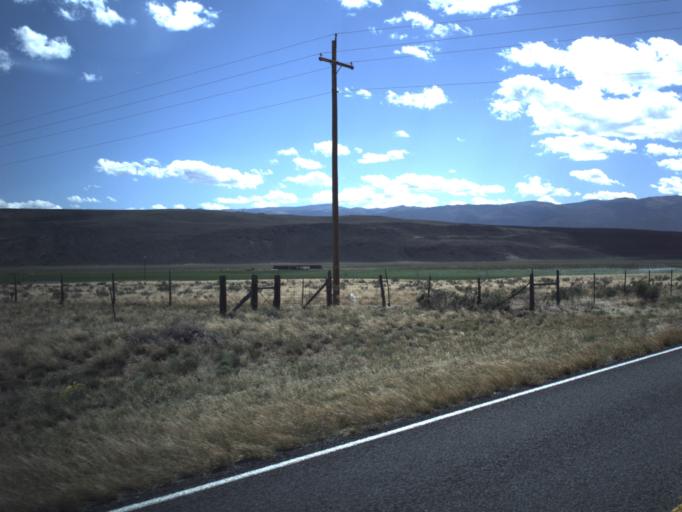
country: US
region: Utah
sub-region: Iron County
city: Enoch
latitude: 37.8901
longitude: -113.0316
